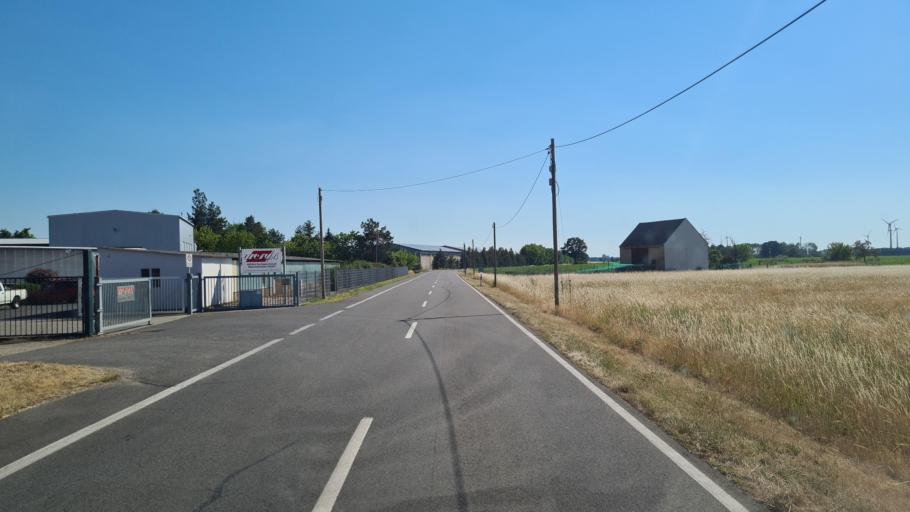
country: DE
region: Saxony-Anhalt
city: Annaburg
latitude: 51.6935
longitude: 12.9943
